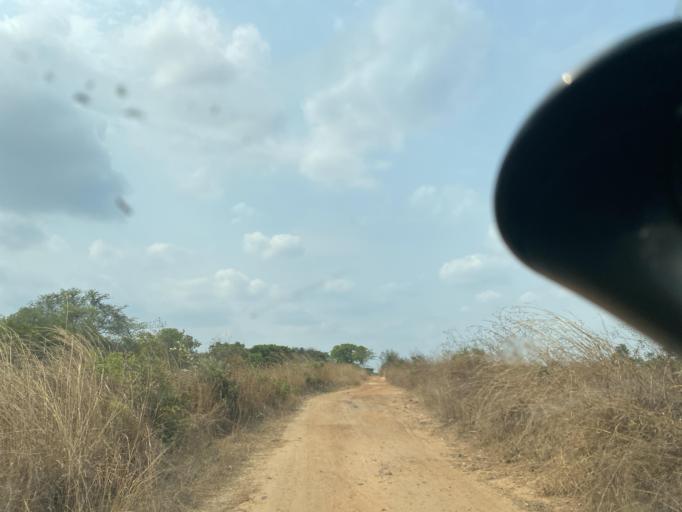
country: ZM
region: Lusaka
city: Lusaka
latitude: -15.1385
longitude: 28.3676
